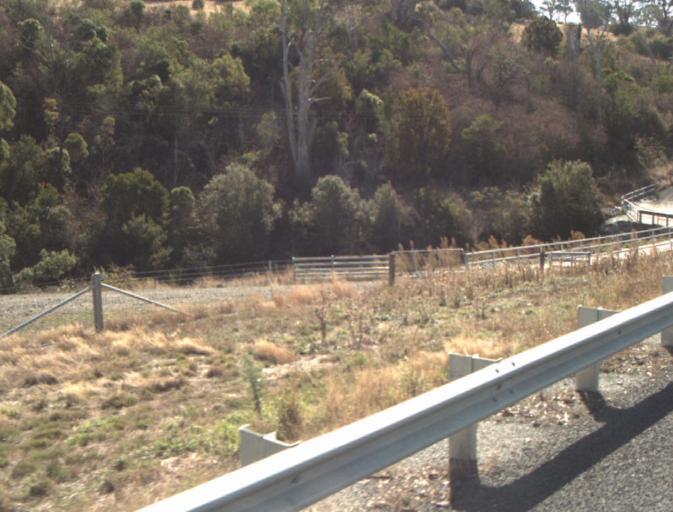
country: AU
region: Tasmania
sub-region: Launceston
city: Mayfield
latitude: -41.3627
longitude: 147.1073
